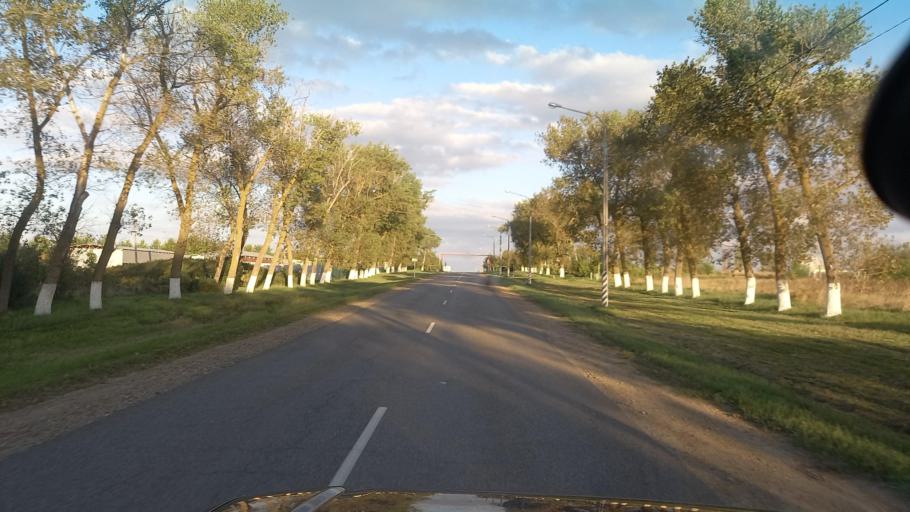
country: RU
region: Krasnodarskiy
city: Krymsk
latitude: 44.9392
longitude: 37.9411
